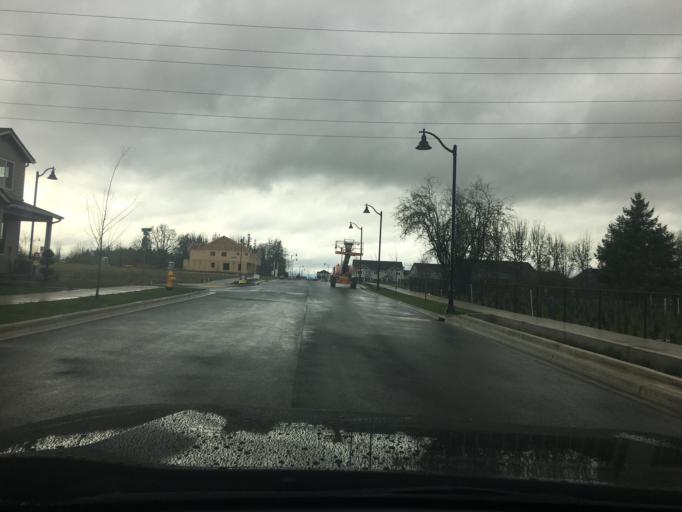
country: US
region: Oregon
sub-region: Washington County
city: Bethany
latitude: 45.5721
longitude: -122.8436
